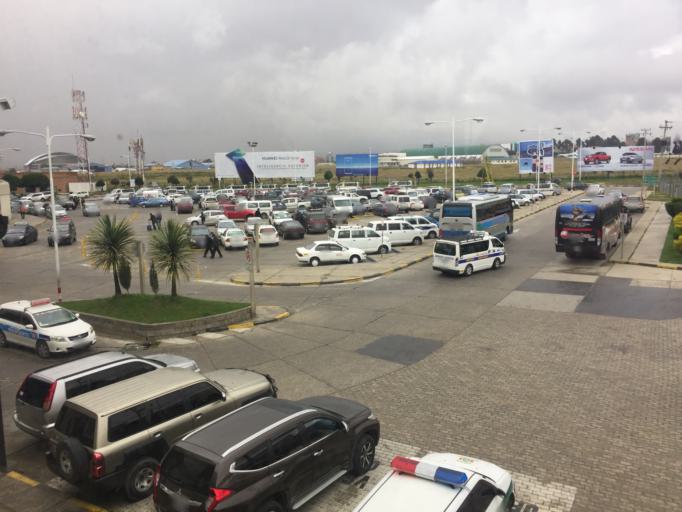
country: BO
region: La Paz
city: La Paz
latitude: -16.5094
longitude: -68.1760
